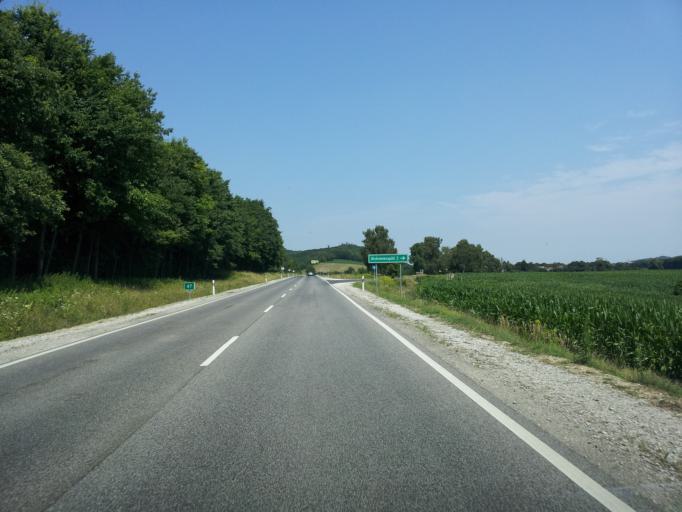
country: HU
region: Zala
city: Zalaegerszeg
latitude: 46.8355
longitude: 16.9283
